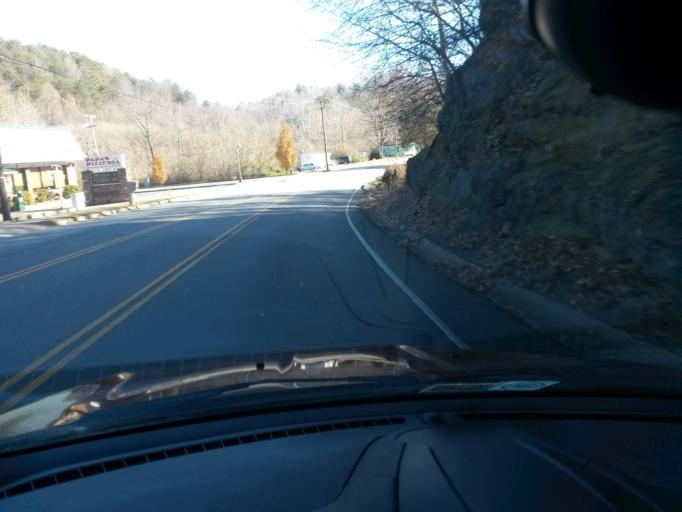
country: US
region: Virginia
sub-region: Henry County
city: Bassett
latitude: 36.7660
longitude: -80.0003
